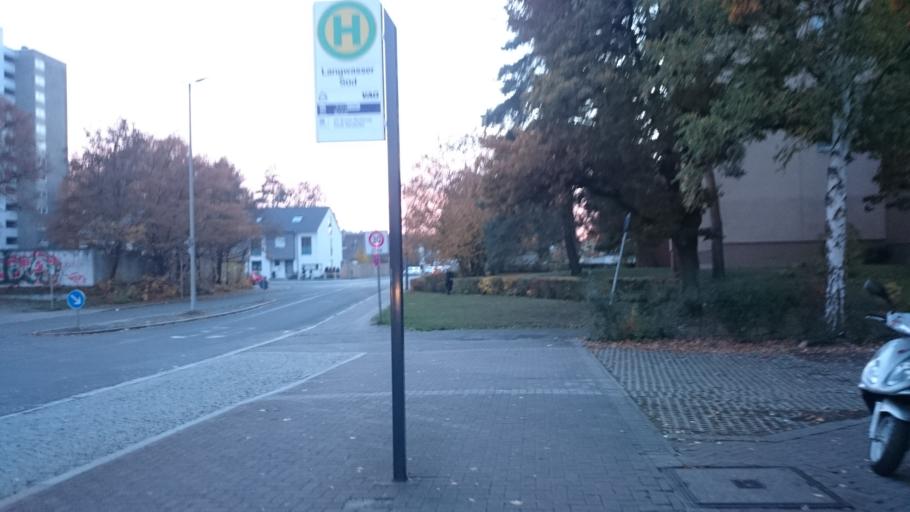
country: DE
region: Bavaria
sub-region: Regierungsbezirk Mittelfranken
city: Wendelstein
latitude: 49.3982
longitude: 11.1412
